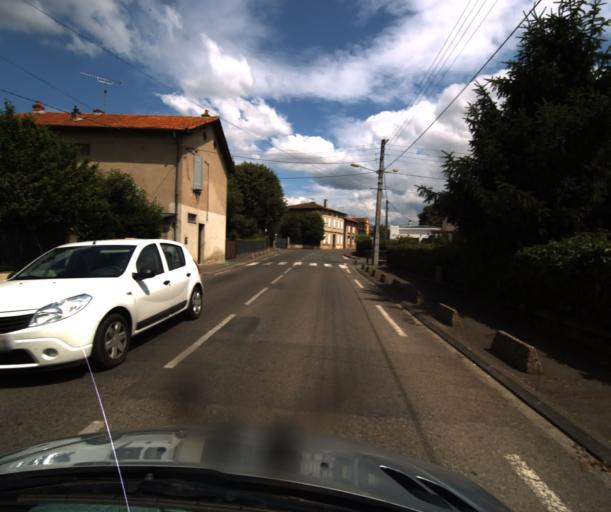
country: FR
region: Midi-Pyrenees
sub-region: Departement du Tarn-et-Garonne
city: Montauban
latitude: 44.0094
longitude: 1.3492
